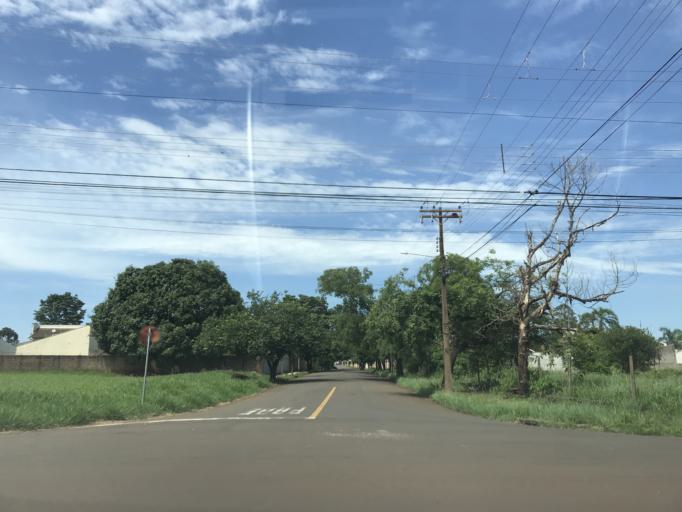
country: BR
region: Parana
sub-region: Londrina
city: Londrina
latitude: -23.3476
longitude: -51.1601
